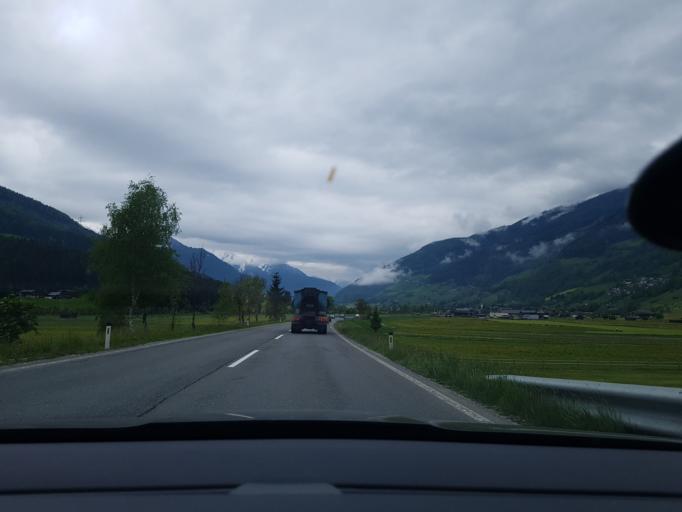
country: AT
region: Salzburg
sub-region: Politischer Bezirk Zell am See
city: Bramberg am Wildkogel
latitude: 47.2753
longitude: 12.3710
